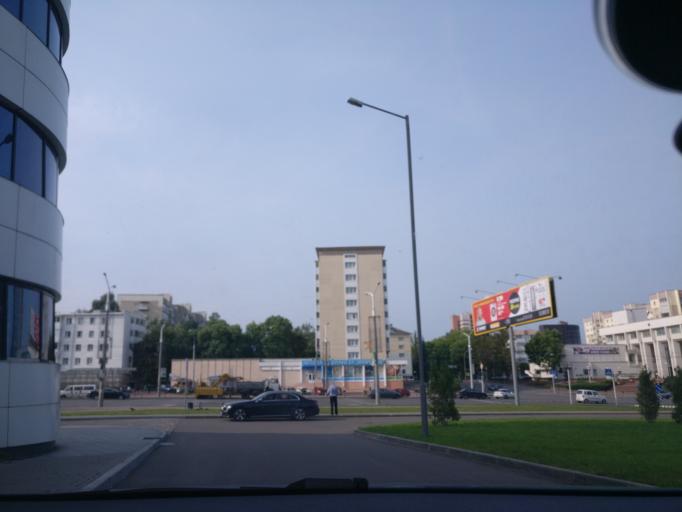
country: BY
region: Minsk
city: Minsk
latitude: 53.8926
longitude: 27.5296
